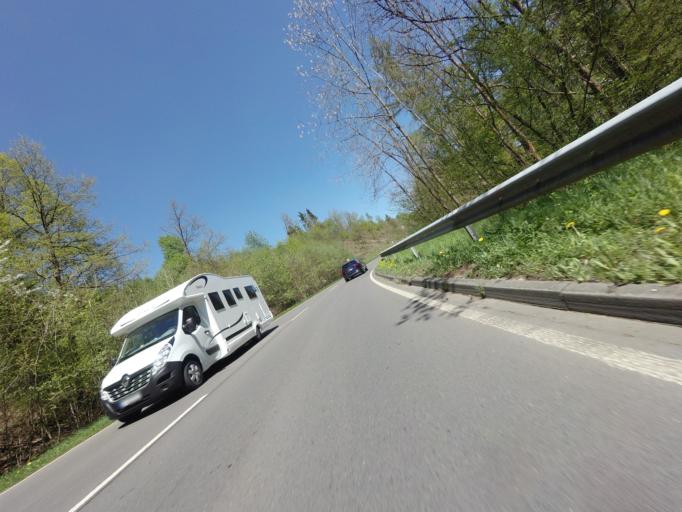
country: DE
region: North Rhine-Westphalia
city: Kreuztal
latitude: 51.0021
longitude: 7.9387
